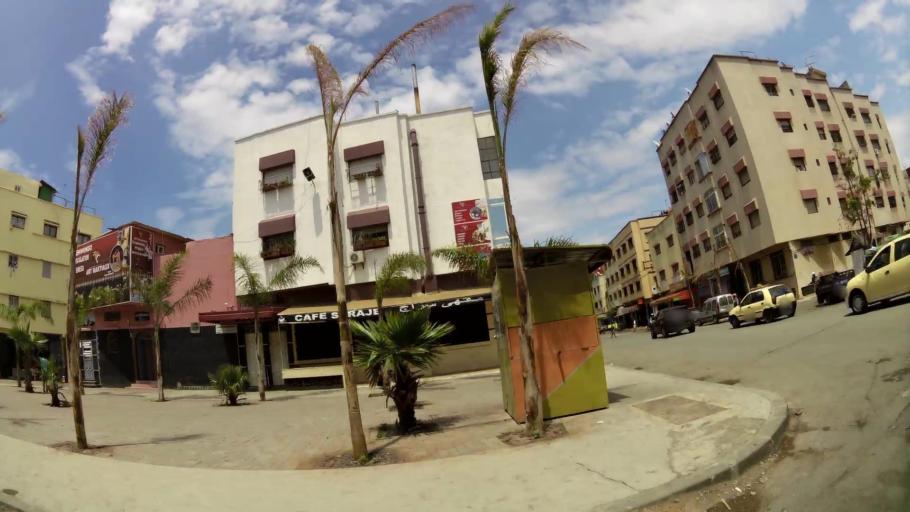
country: MA
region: Rabat-Sale-Zemmour-Zaer
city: Sale
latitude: 34.0486
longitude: -6.8180
